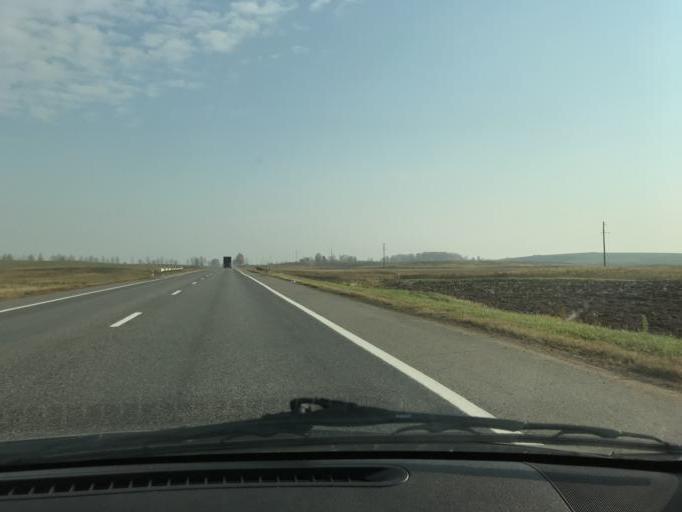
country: BY
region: Vitebsk
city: Chashniki
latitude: 55.0131
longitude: 29.0890
